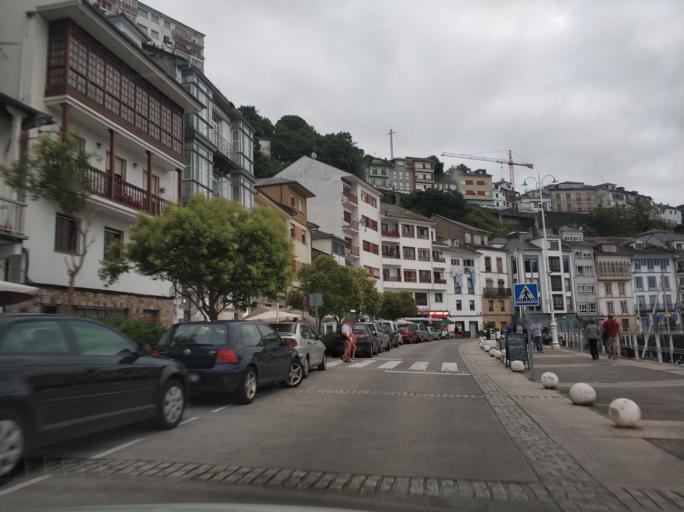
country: ES
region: Asturias
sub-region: Province of Asturias
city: Navia
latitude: 43.5460
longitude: -6.5319
